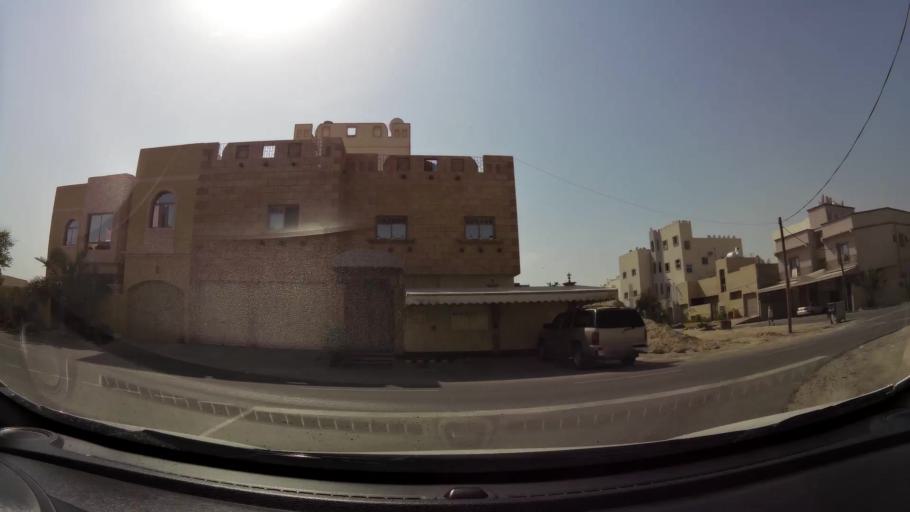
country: BH
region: Manama
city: Jidd Hafs
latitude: 26.2082
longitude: 50.4638
